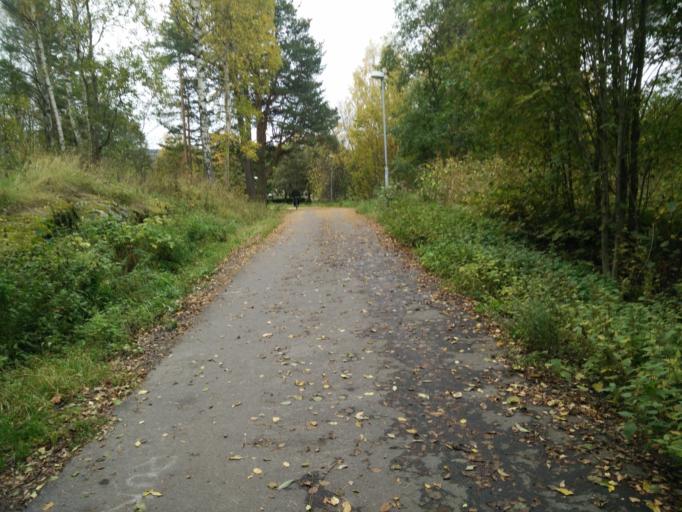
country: SE
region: Vaesternorrland
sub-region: Sundsvalls Kommun
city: Sundsvall
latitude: 62.3987
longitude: 17.2716
